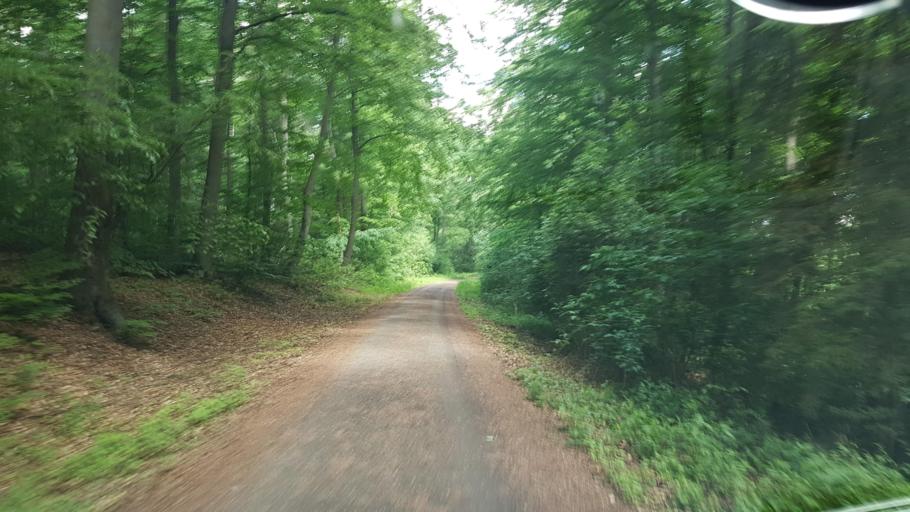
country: DE
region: Lower Saxony
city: Warberg
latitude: 52.1744
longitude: 10.9036
